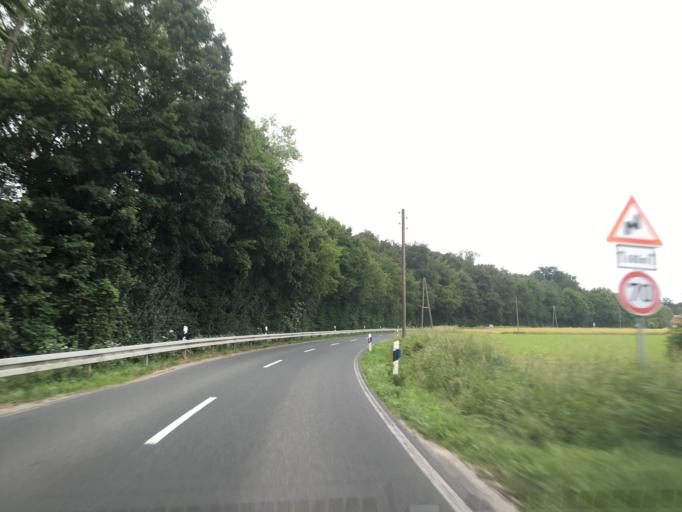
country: DE
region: North Rhine-Westphalia
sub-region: Regierungsbezirk Munster
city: Laer
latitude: 52.0827
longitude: 7.3447
